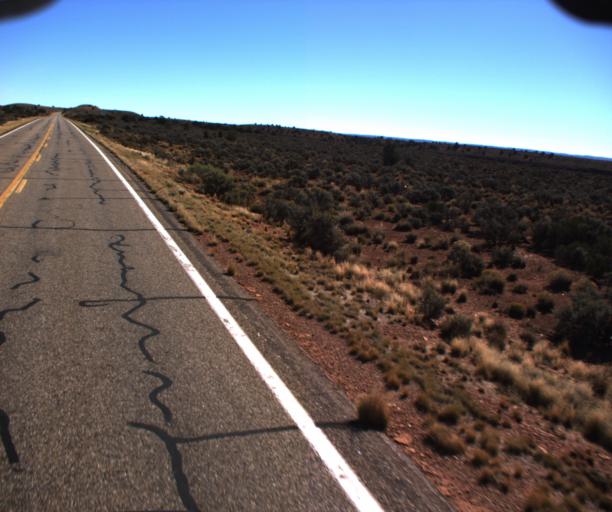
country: US
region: Arizona
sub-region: Coconino County
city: Fredonia
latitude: 36.9078
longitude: -112.4087
